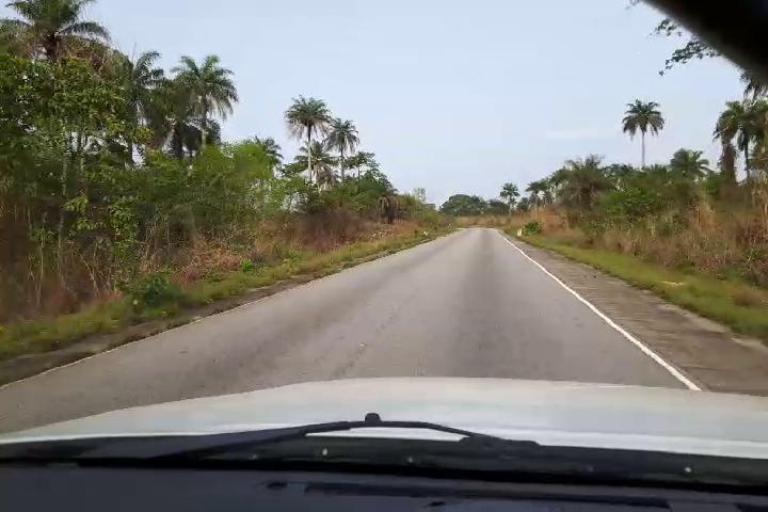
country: SL
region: Southern Province
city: Baoma
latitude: 7.9256
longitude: -11.5351
